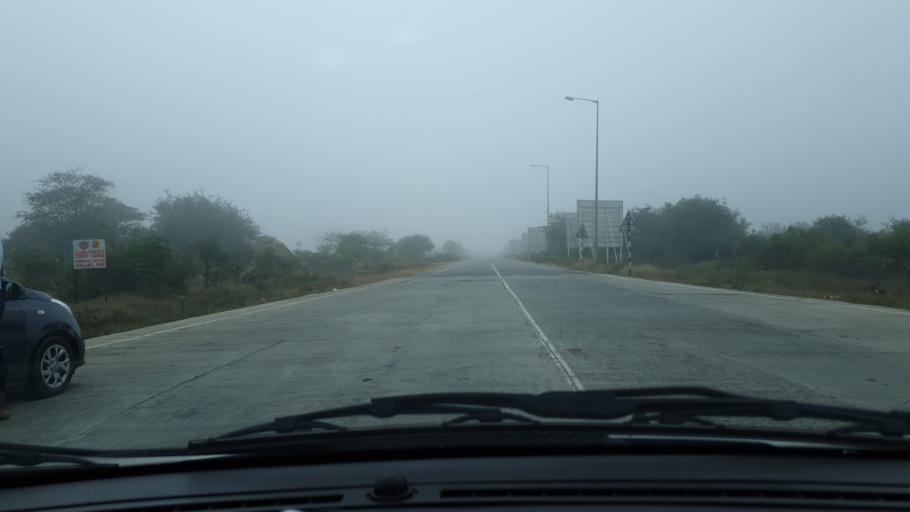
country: IN
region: Telangana
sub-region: Nalgonda
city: Devarkonda
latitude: 16.6111
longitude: 78.6763
